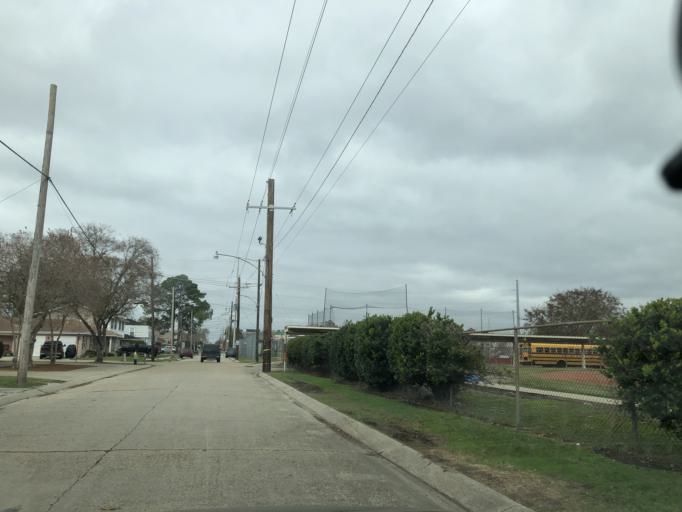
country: US
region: Louisiana
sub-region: Jefferson Parish
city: Metairie
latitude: 29.9906
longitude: -90.1612
